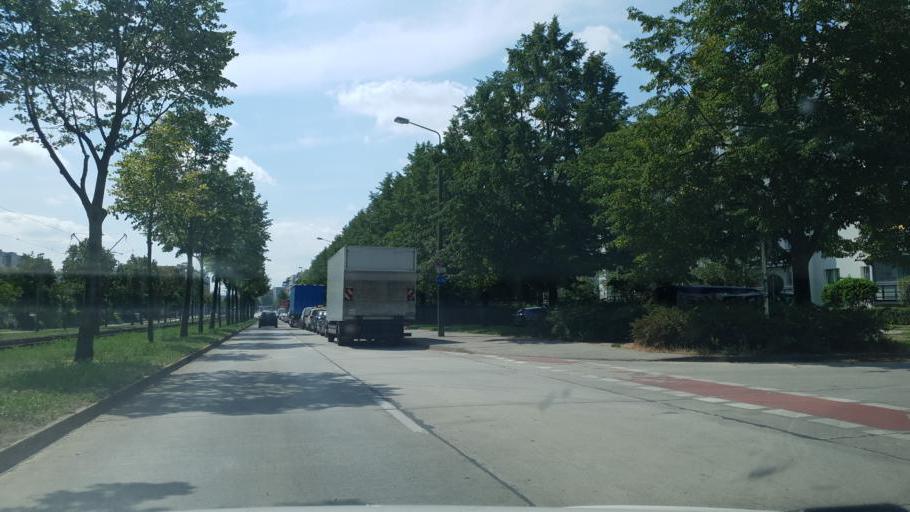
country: DE
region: Berlin
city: Hellersdorf
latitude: 52.5420
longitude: 13.6036
